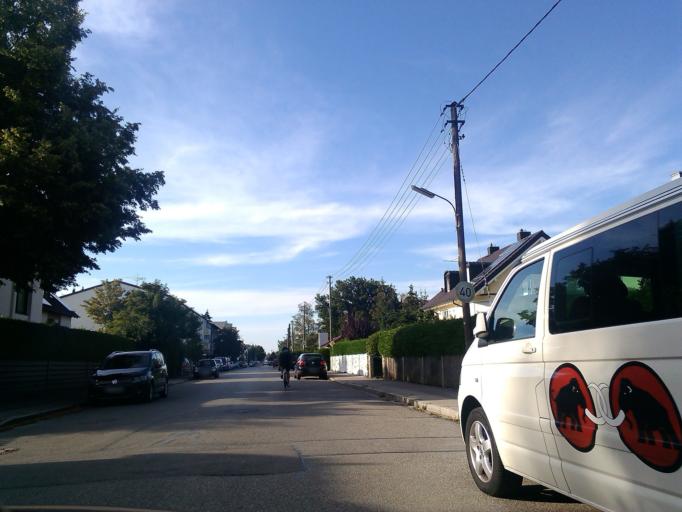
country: DE
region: Bavaria
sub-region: Upper Bavaria
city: Germering
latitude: 48.1206
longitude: 11.3669
